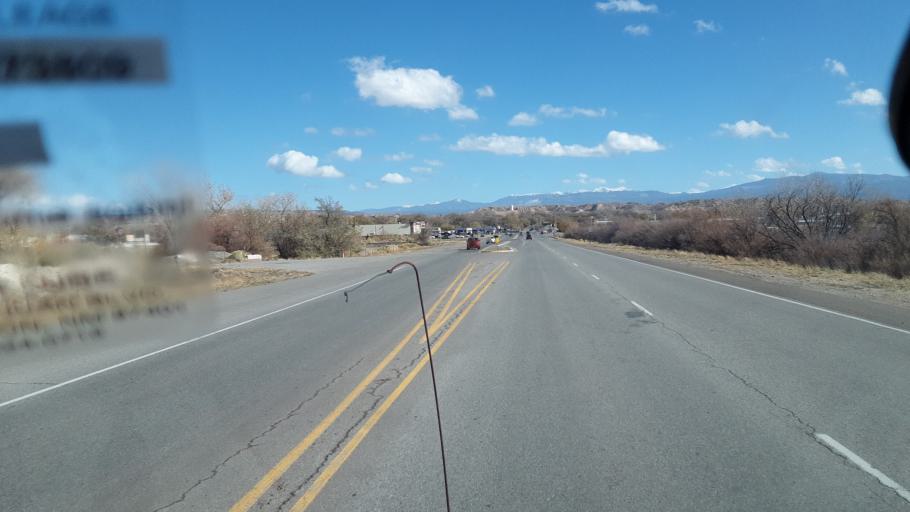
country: US
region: New Mexico
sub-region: Rio Arriba County
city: Espanola
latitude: 36.0082
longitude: -106.0702
